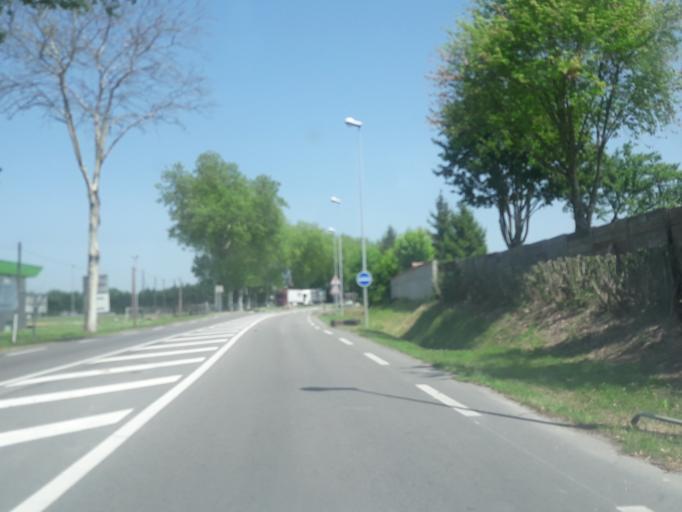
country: FR
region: Rhone-Alpes
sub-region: Departement de l'Ain
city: Mionnay
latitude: 45.8979
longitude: 4.9311
